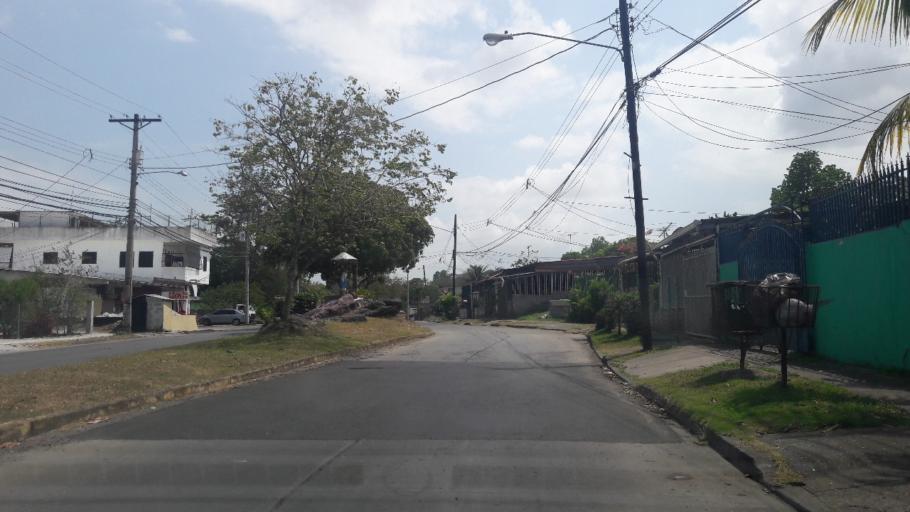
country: PA
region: Panama
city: Alcalde Diaz
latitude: 9.1304
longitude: -79.5476
